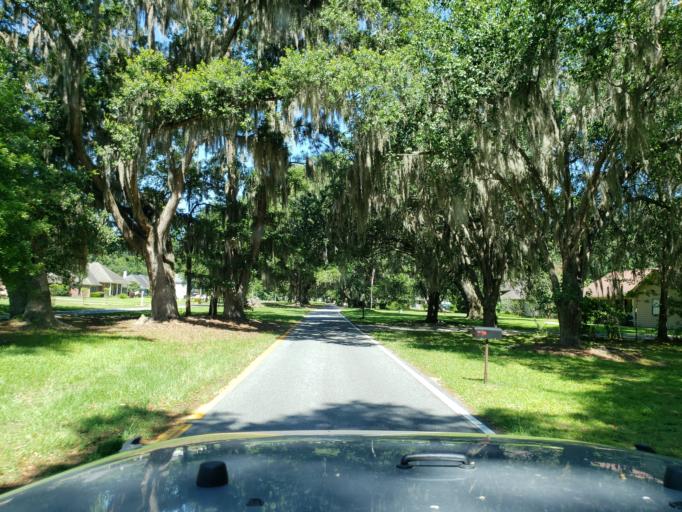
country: US
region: Georgia
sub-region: Chatham County
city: Georgetown
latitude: 31.9712
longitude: -81.2236
